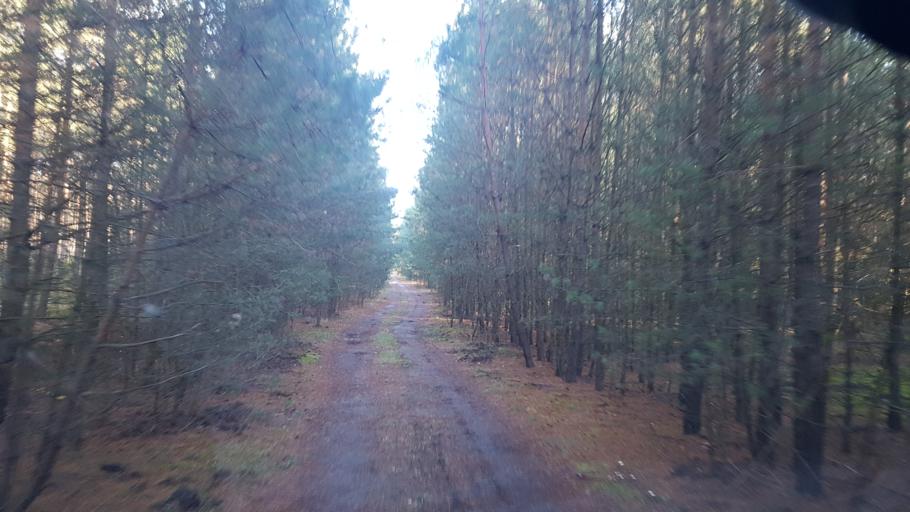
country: DE
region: Brandenburg
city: Crinitz
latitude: 51.7254
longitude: 13.7458
